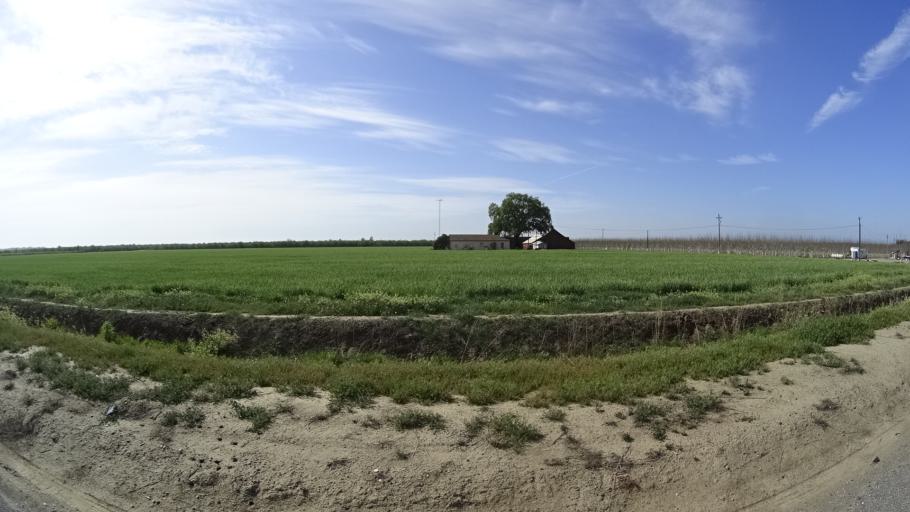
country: US
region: California
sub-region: Glenn County
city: Hamilton City
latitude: 39.6234
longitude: -122.0173
